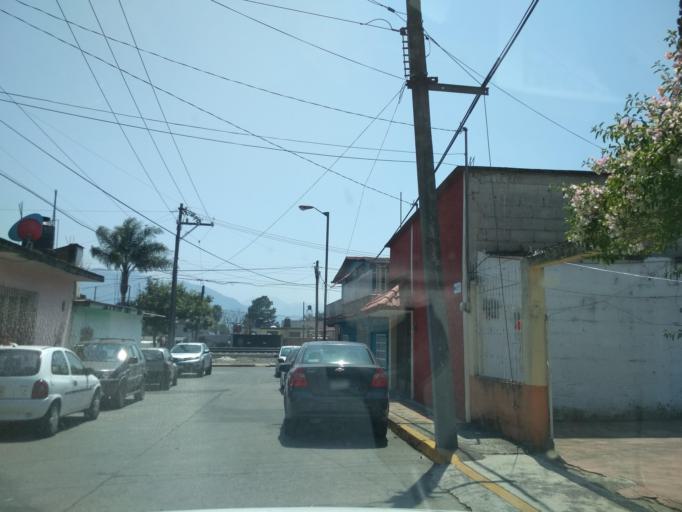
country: MX
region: Veracruz
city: Orizaba
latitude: 18.8482
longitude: -97.0861
